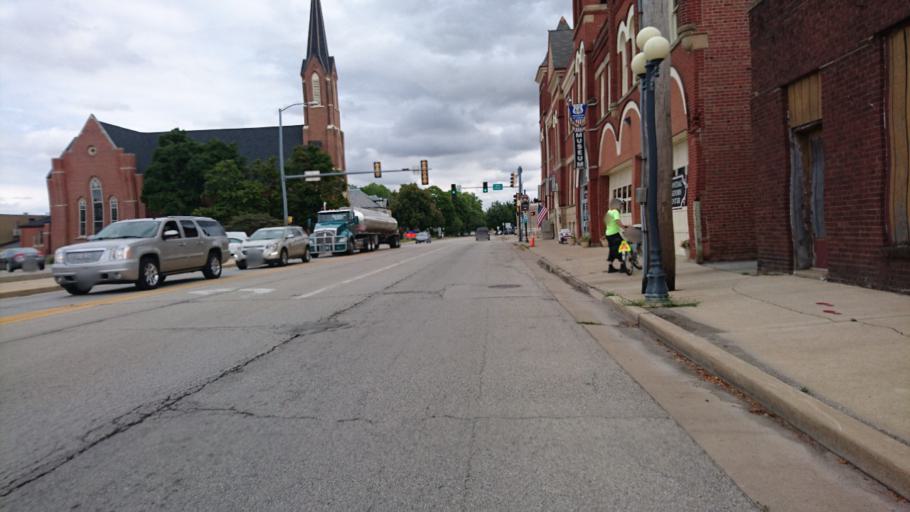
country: US
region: Illinois
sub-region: Livingston County
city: Pontiac
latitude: 40.8811
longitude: -88.6294
